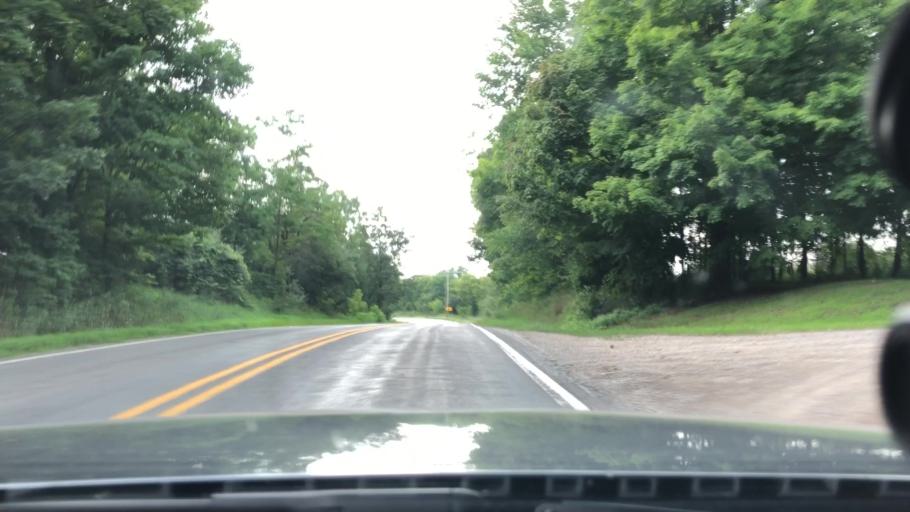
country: US
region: Michigan
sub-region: Washtenaw County
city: Manchester
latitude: 42.1451
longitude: -84.0645
